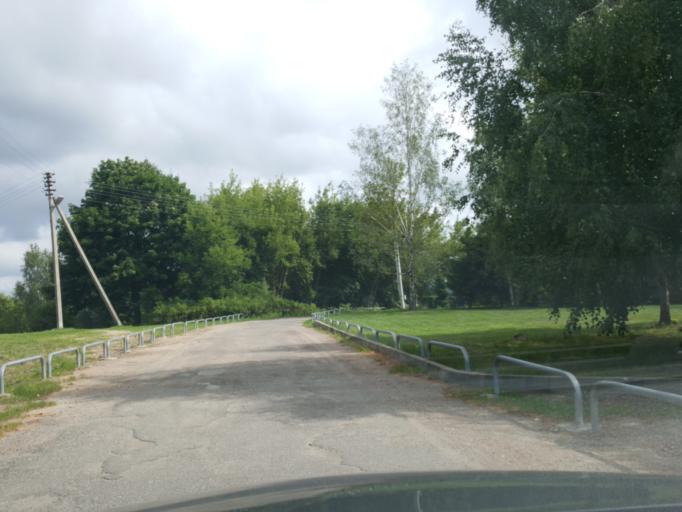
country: LT
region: Alytaus apskritis
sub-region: Alytus
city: Alytus
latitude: 54.4009
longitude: 24.0376
